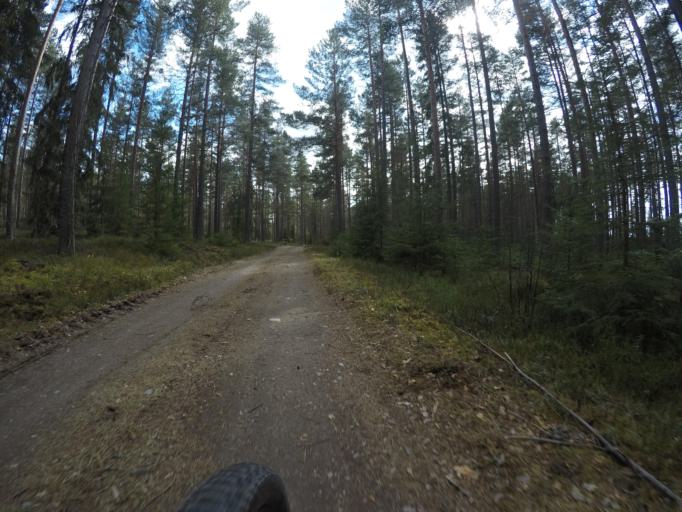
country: SE
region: Vaestmanland
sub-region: Kungsors Kommun
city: Kungsoer
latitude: 59.3441
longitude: 16.1075
